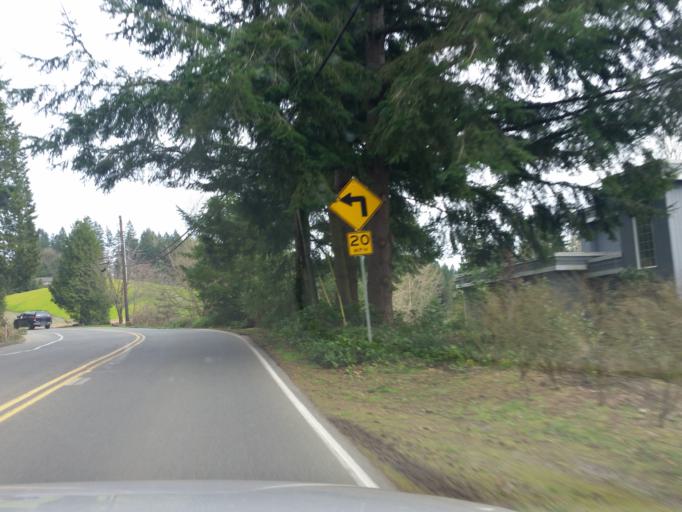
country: US
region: Washington
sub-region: King County
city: Woodinville
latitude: 47.7526
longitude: -122.1351
